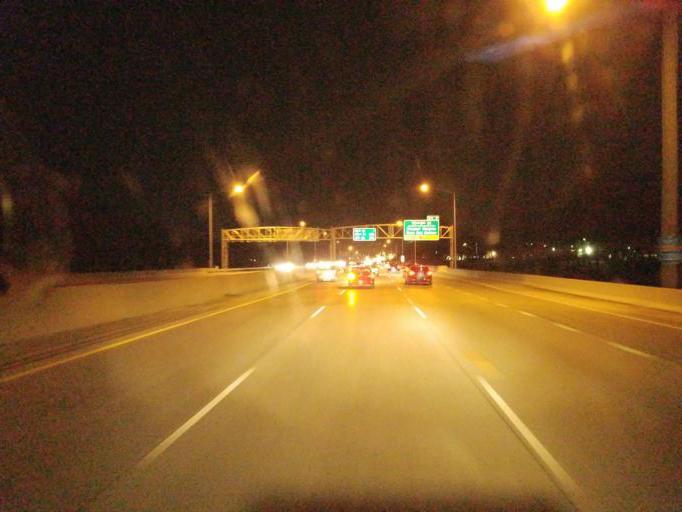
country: US
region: Iowa
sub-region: Polk County
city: Clive
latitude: 41.5933
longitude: -93.7281
